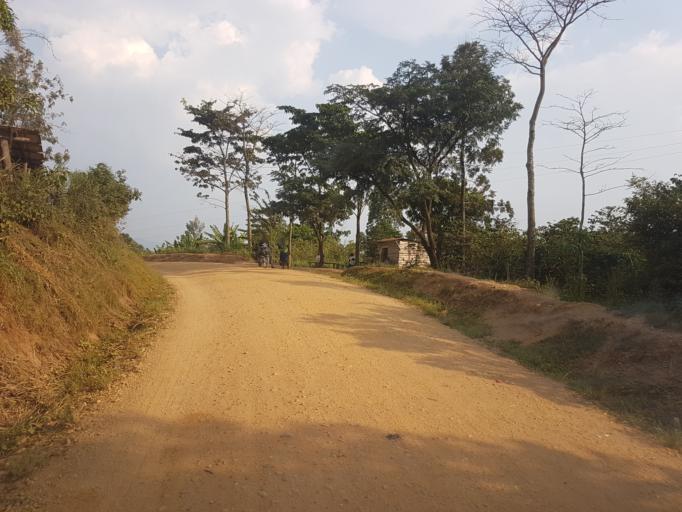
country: UG
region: Western Region
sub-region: Rukungiri District
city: Rukungiri
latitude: -0.6499
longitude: 29.8510
